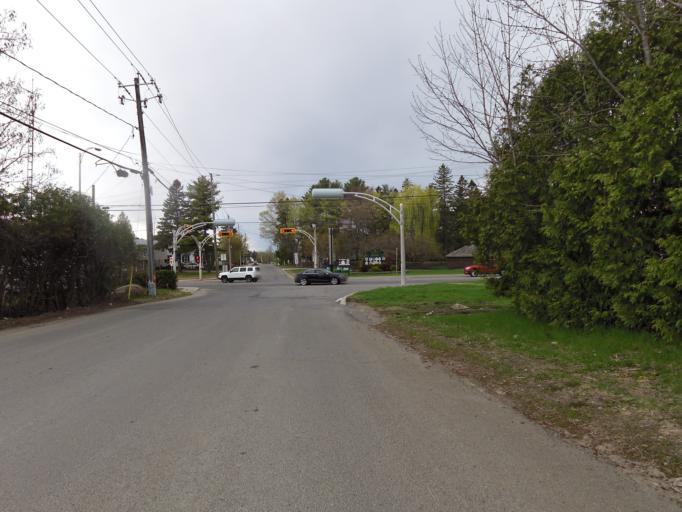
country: CA
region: Ontario
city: Hawkesbury
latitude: 45.6264
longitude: -74.5904
